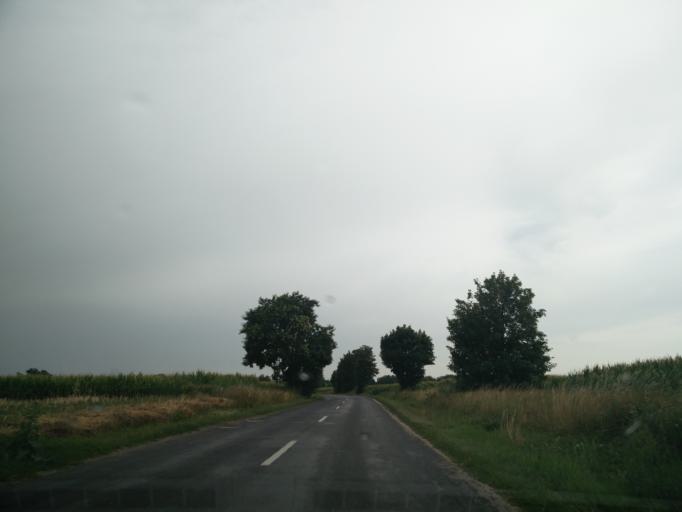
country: HU
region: Fejer
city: Bicske
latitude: 47.4327
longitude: 18.6554
